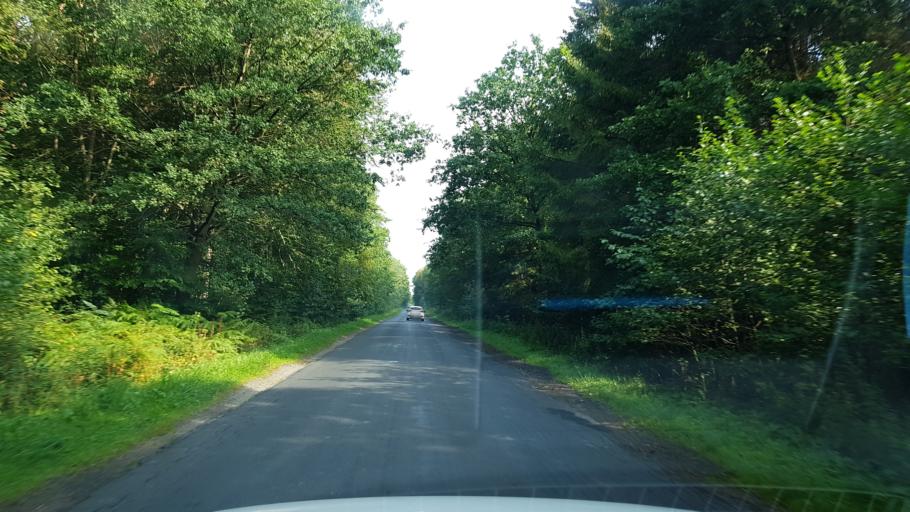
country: PL
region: West Pomeranian Voivodeship
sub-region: Powiat slawienski
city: Slawno
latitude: 54.4208
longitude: 16.6160
